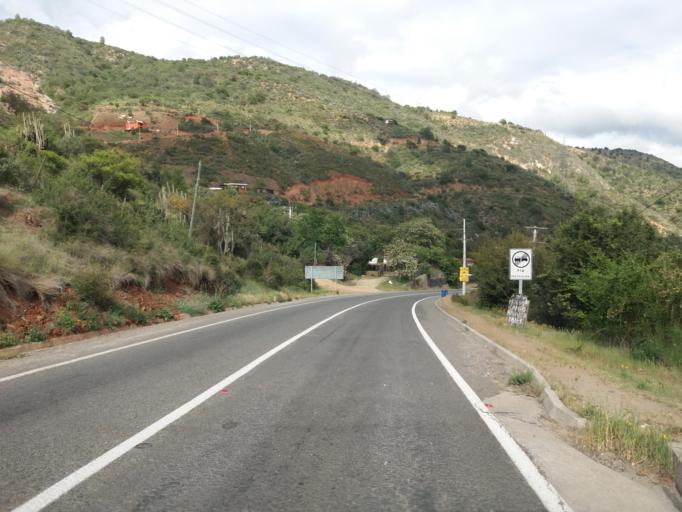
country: CL
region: Valparaiso
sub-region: Provincia de Marga Marga
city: Limache
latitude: -33.0633
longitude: -71.0693
